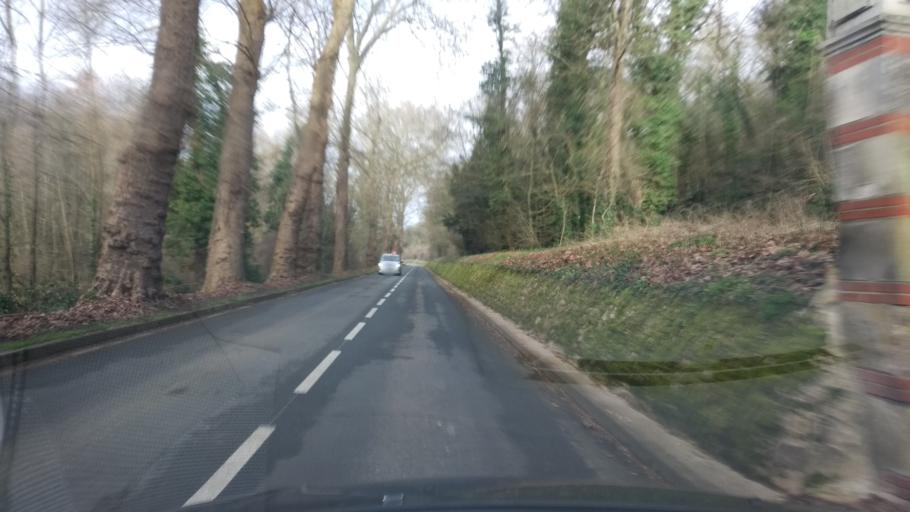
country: FR
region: Poitou-Charentes
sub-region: Departement de la Vienne
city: Poitiers
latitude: 46.6048
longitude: 0.3495
